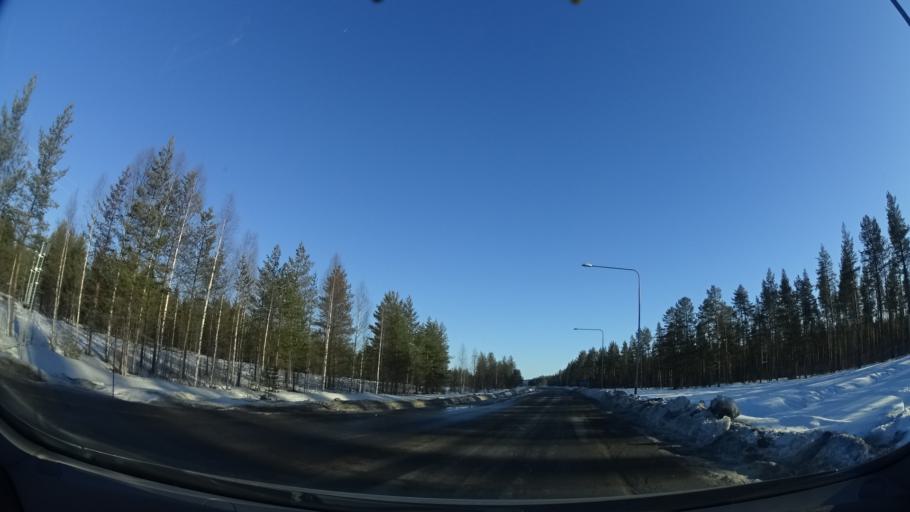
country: SE
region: Vaesterbotten
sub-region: Skelleftea Kommun
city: Langsele
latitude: 65.0533
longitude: 20.0576
